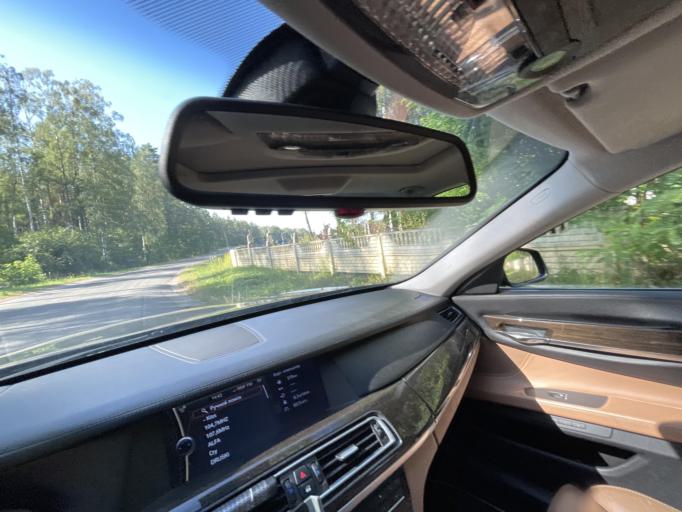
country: BY
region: Grodnenskaya
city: Hrodna
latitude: 53.7522
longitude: 23.9745
